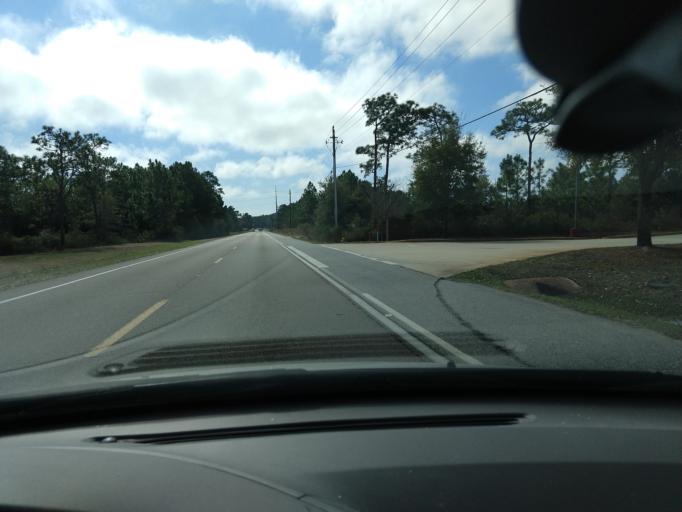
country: US
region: Florida
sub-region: Walton County
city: Miramar Beach
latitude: 30.3834
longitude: -86.3047
